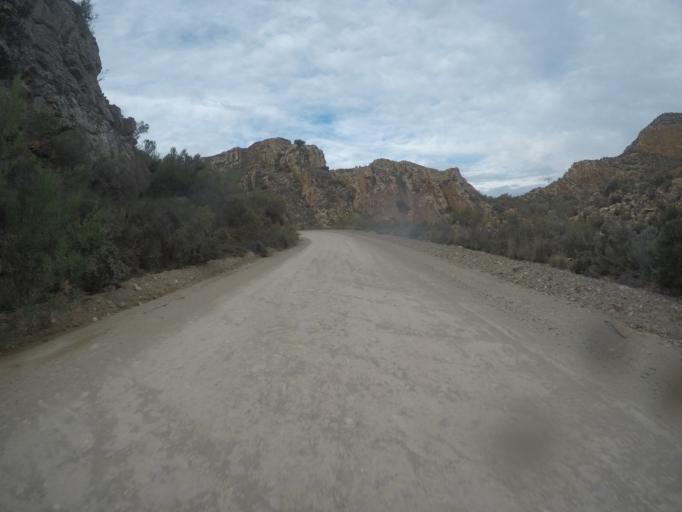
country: ZA
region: Eastern Cape
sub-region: Cacadu District Municipality
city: Willowmore
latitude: -33.5086
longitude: 23.6367
